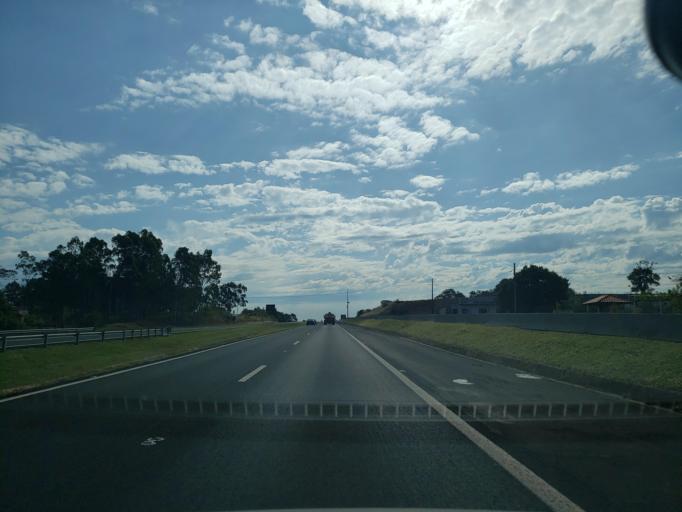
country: BR
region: Sao Paulo
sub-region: Pirajui
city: Pirajui
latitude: -21.9819
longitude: -49.4470
